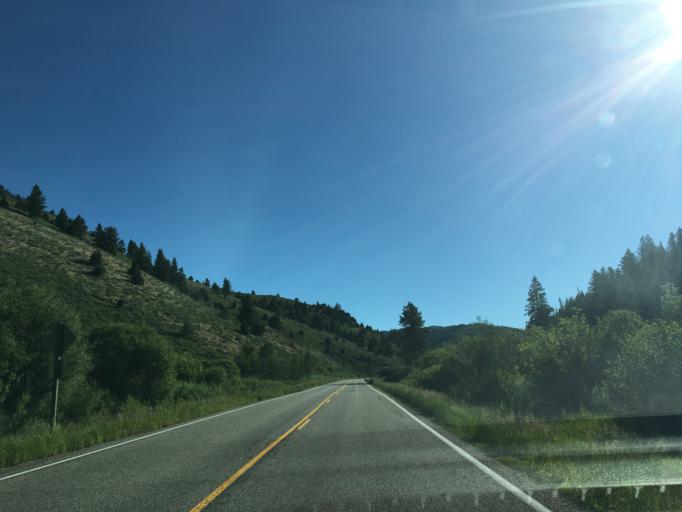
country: US
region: Idaho
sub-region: Teton County
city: Victor
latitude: 43.5551
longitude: -111.2878
